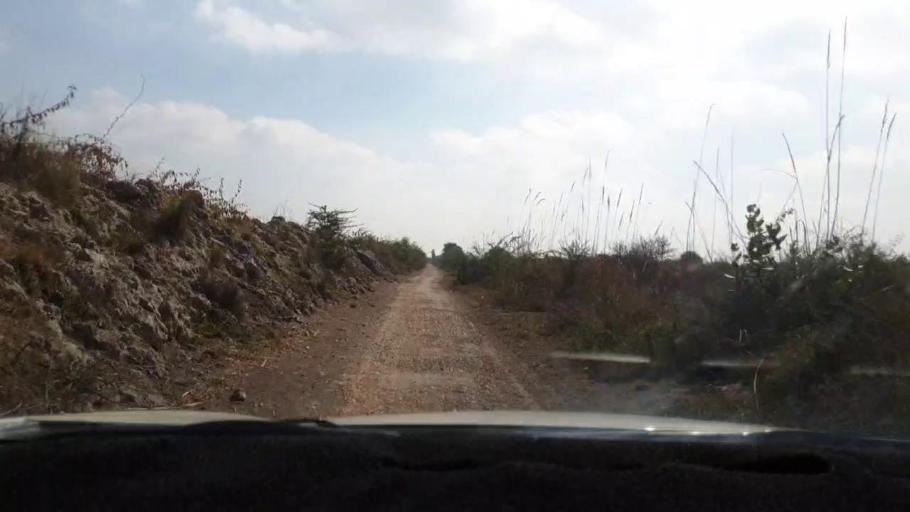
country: PK
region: Sindh
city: Berani
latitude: 25.7705
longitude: 68.9793
